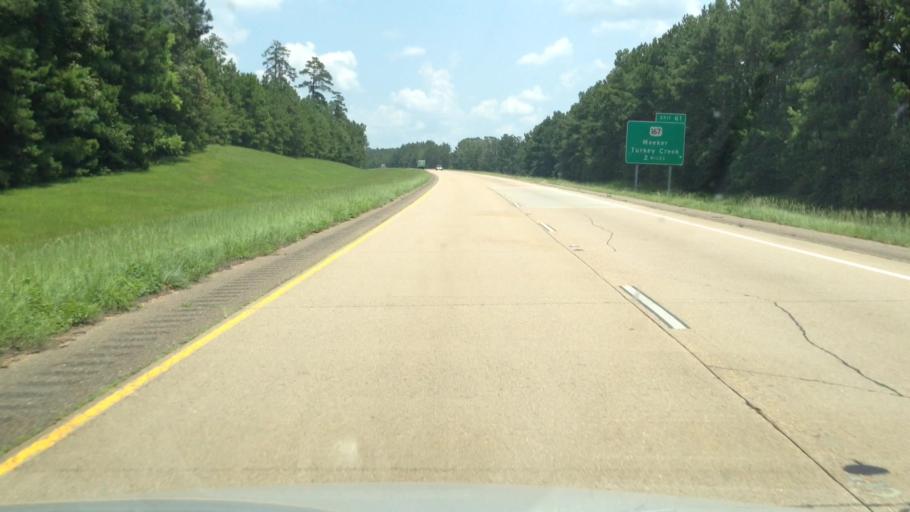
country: US
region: Louisiana
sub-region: Rapides Parish
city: Lecompte
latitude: 31.0317
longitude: -92.4097
